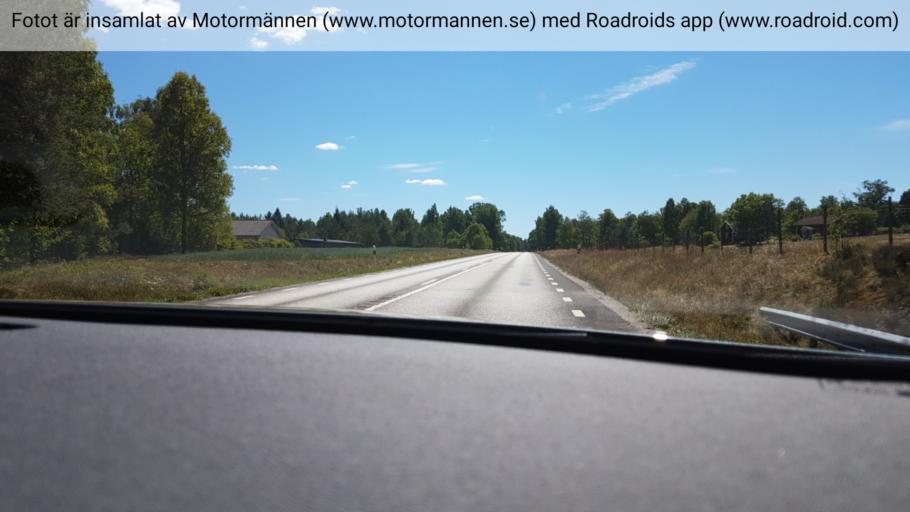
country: SE
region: Joenkoeping
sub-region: Gnosjo Kommun
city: Gnosjoe
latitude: 57.5425
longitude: 13.6897
